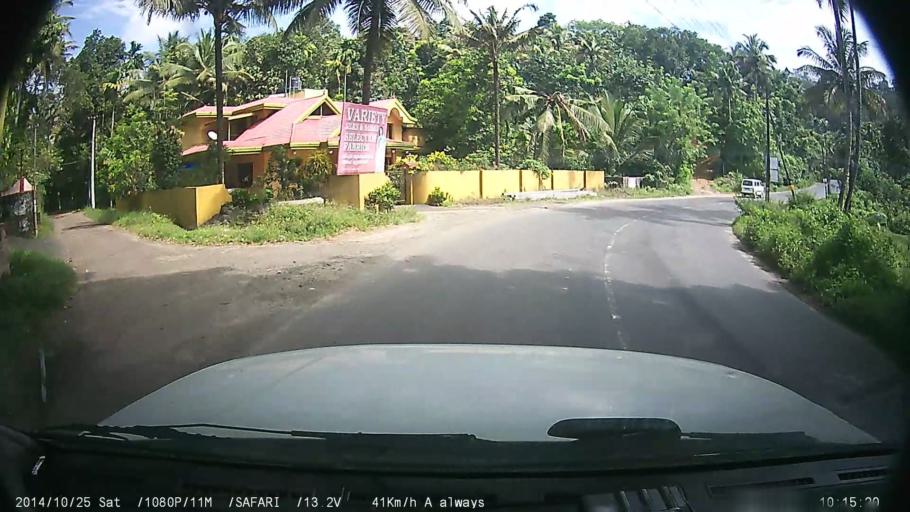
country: IN
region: Kerala
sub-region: Ernakulam
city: Piravam
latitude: 9.8721
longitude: 76.5958
